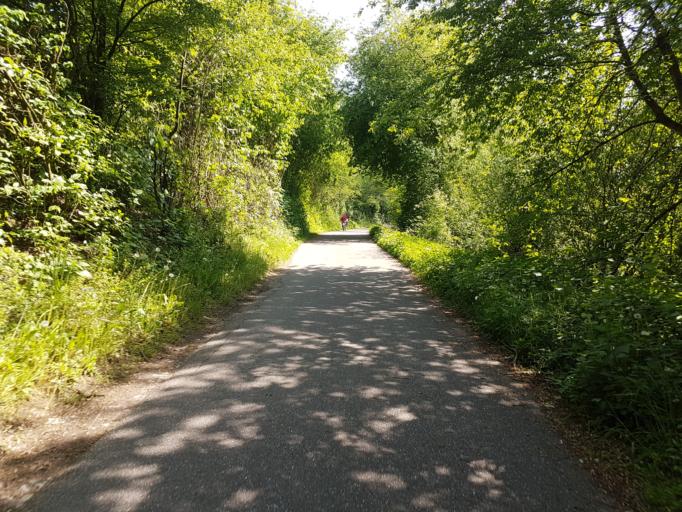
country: DE
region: Baden-Wuerttemberg
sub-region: Regierungsbezirk Stuttgart
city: Besigheim
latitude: 48.9761
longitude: 9.1488
